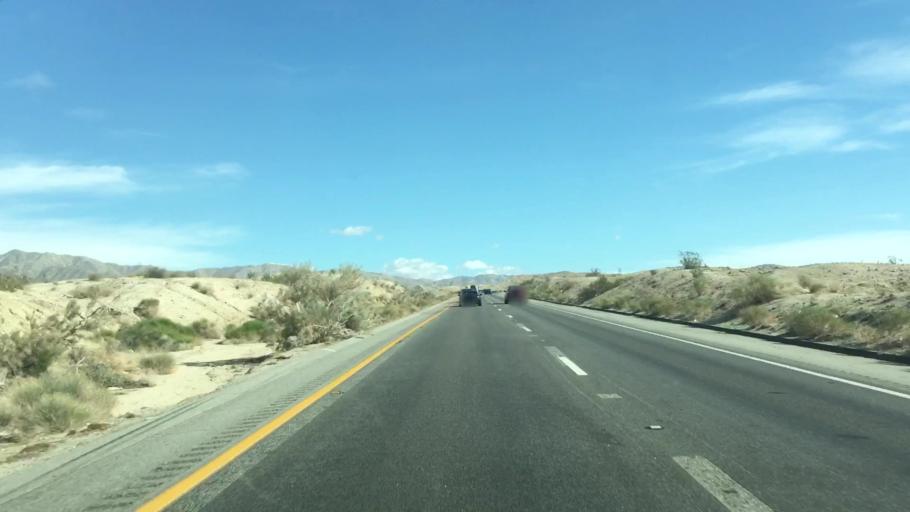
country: US
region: California
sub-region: Riverside County
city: Thermal
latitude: 33.6986
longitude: -116.0951
